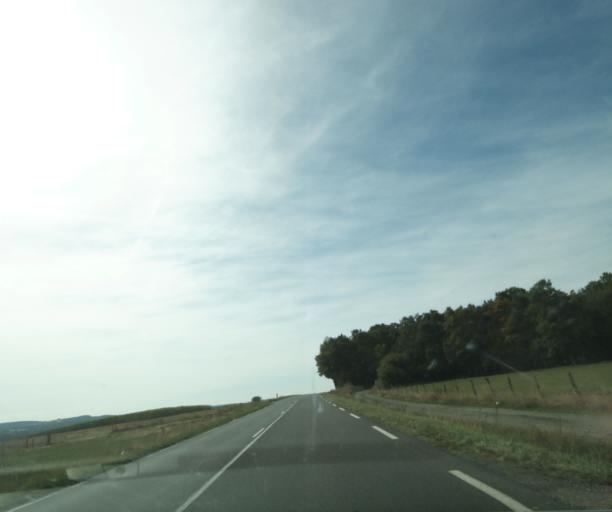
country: FR
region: Auvergne
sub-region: Departement de l'Allier
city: Saint-Gerand-le-Puy
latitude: 46.1977
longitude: 3.4956
